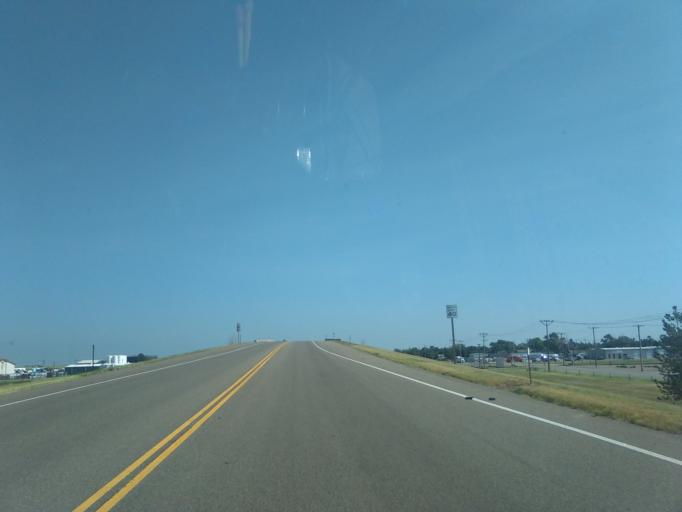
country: US
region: Kansas
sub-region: Sherman County
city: Goodland
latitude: 39.3387
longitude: -101.7266
